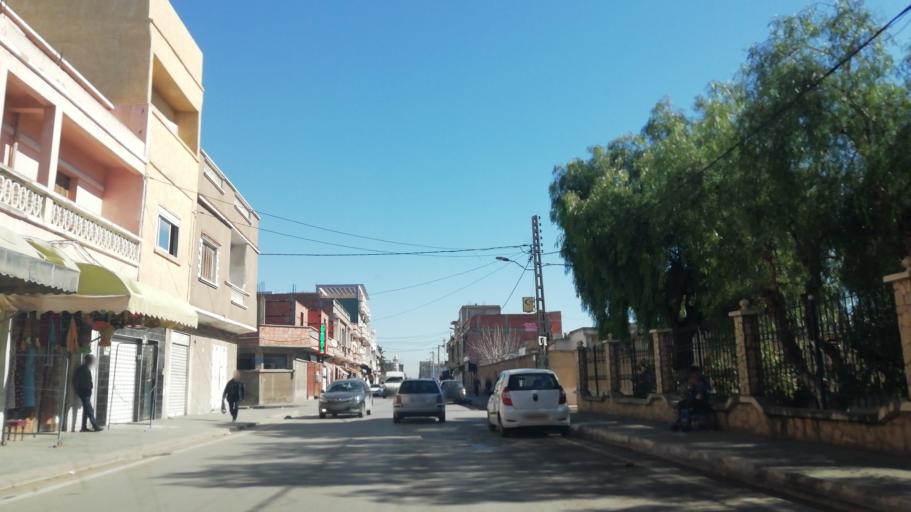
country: DZ
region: Oran
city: Es Senia
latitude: 35.6518
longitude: -0.6236
